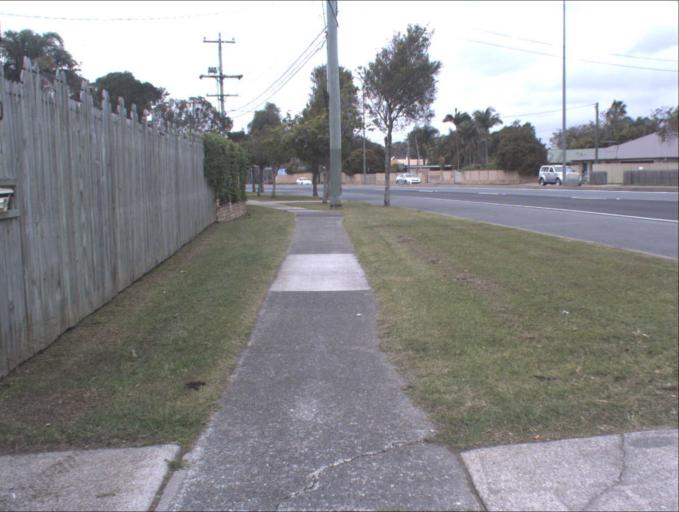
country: AU
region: Queensland
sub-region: Logan
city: Waterford West
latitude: -27.6904
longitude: 153.1264
